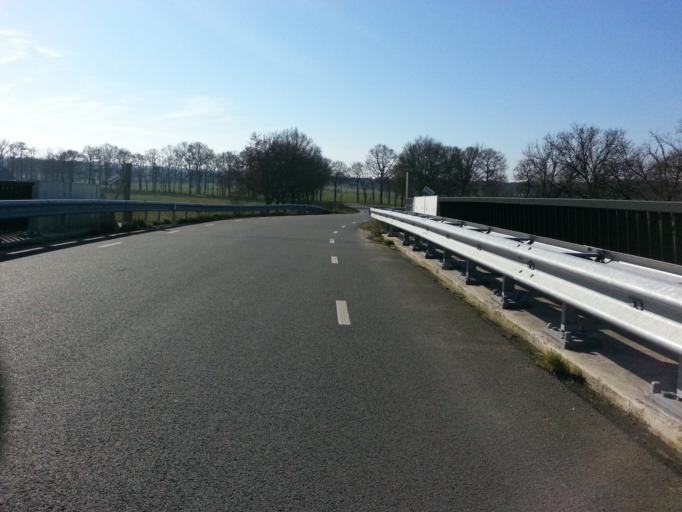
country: NL
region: Utrecht
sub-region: Gemeente Utrechtse Heuvelrug
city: Overberg
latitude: 52.0509
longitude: 5.4562
